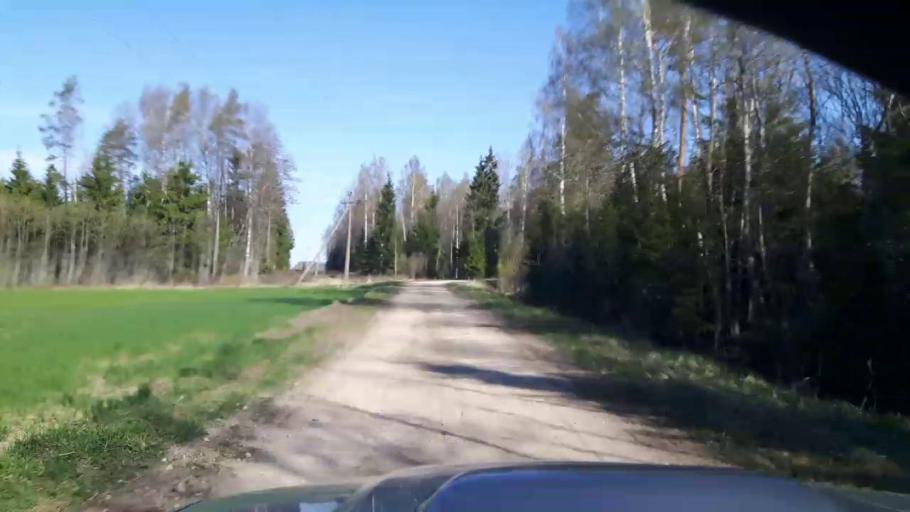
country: EE
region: Paernumaa
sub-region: Tootsi vald
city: Tootsi
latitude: 58.5161
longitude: 24.9282
